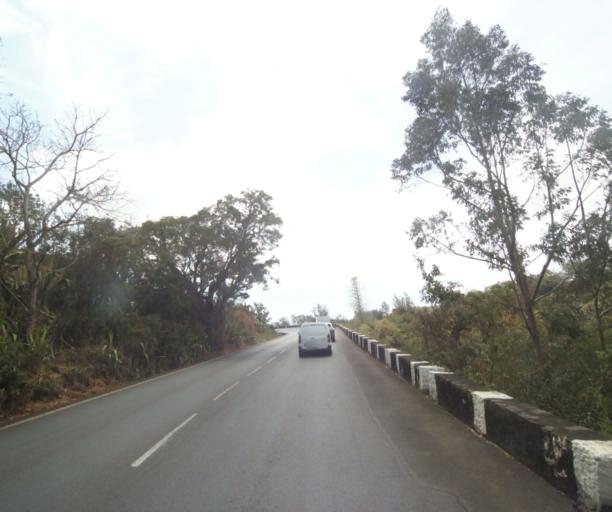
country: RE
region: Reunion
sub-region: Reunion
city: Trois-Bassins
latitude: -21.0700
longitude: 55.2686
